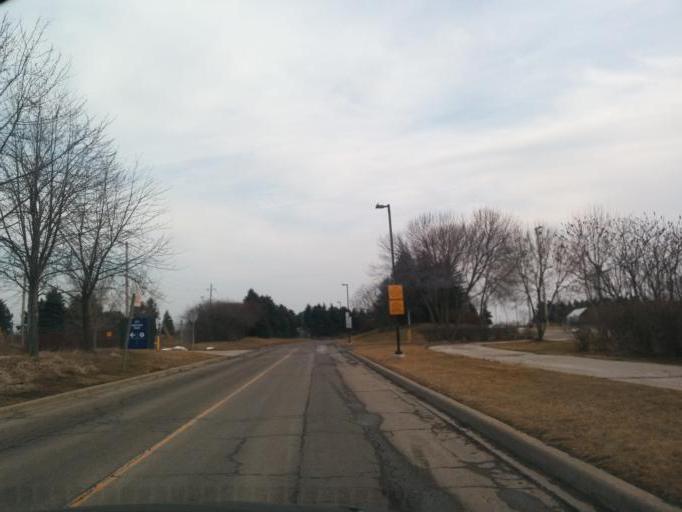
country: CA
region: Ontario
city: Etobicoke
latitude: 43.5725
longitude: -79.5576
